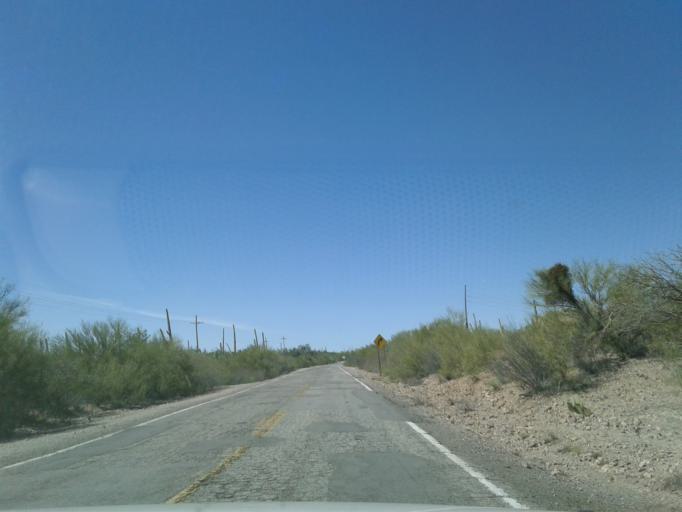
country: US
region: Arizona
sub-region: Pima County
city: Avra Valley
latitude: 32.3780
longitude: -111.4833
